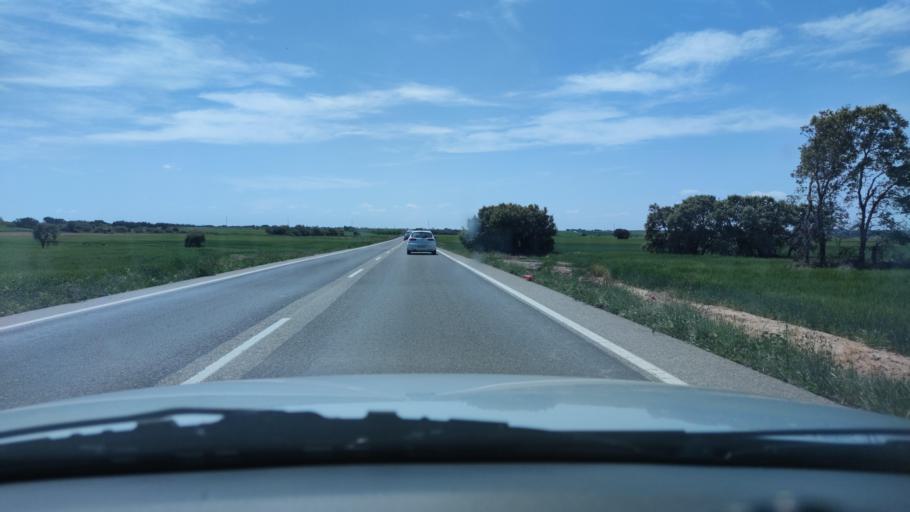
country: ES
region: Catalonia
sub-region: Provincia de Lleida
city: Mont-roig del Camp
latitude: 41.7377
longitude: 1.2178
